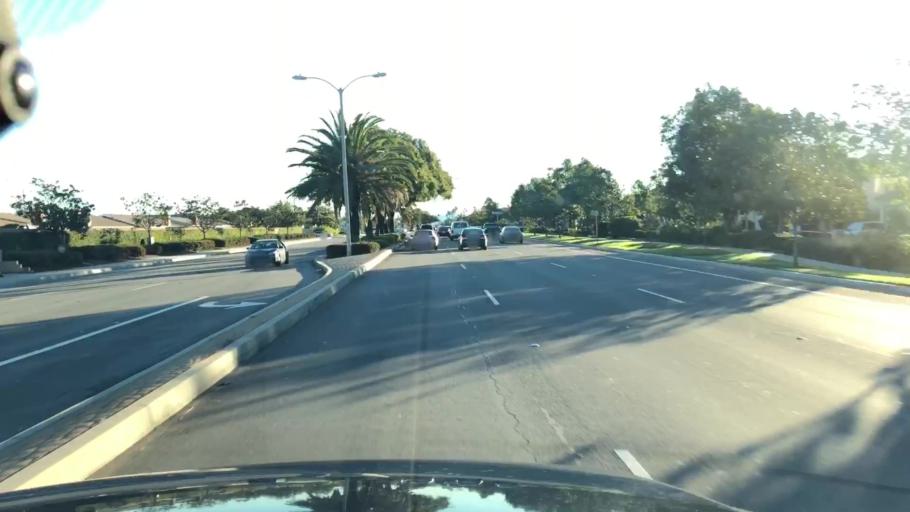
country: US
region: California
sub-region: Ventura County
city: El Rio
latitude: 34.2189
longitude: -119.1650
